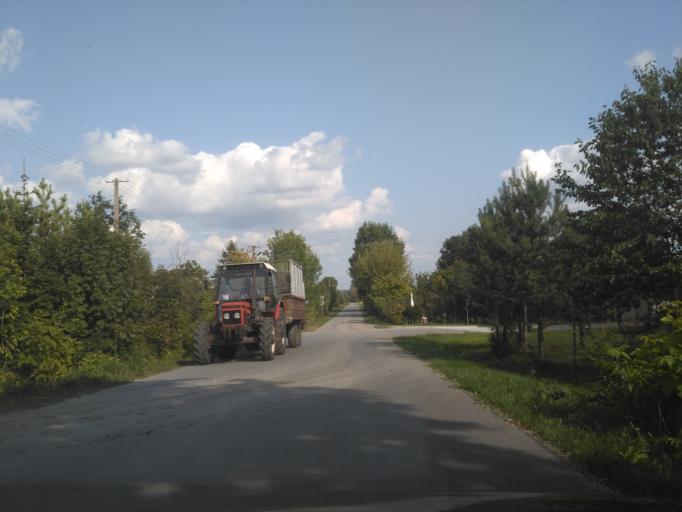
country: PL
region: Lublin Voivodeship
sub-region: Powiat chelmski
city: Pokrowka
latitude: 51.0762
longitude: 23.4804
